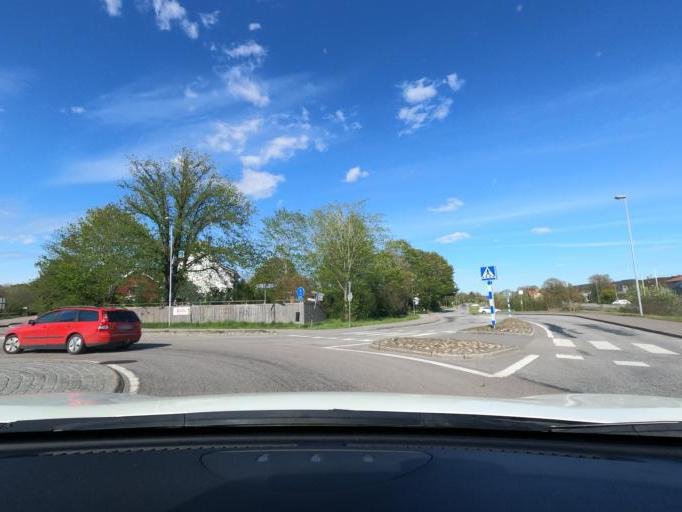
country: SE
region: Vaestra Goetaland
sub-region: Harryda Kommun
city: Ravlanda
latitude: 57.6541
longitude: 12.4959
